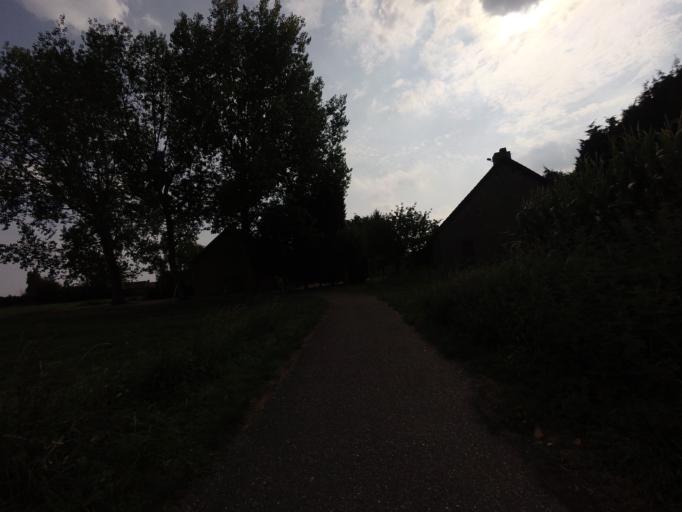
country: BE
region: Flanders
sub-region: Provincie Antwerpen
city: Aartselaar
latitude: 51.1262
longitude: 4.3829
